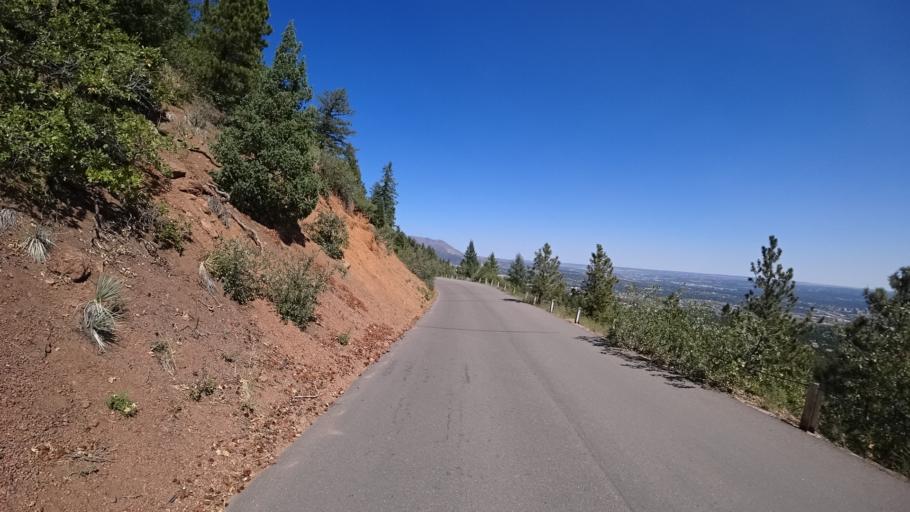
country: US
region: Colorado
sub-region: El Paso County
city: Colorado Springs
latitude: 38.8008
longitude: -104.8767
